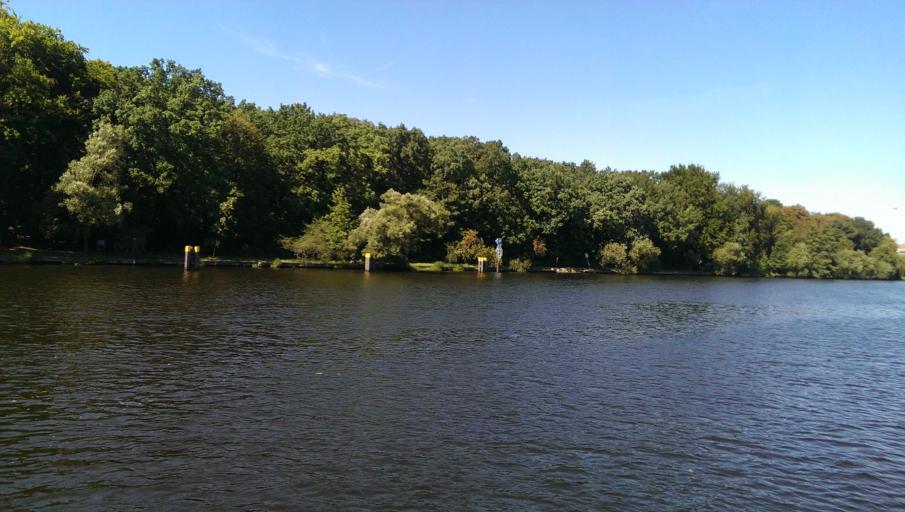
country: DE
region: Berlin
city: Baumschulenweg
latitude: 52.4750
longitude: 13.4955
